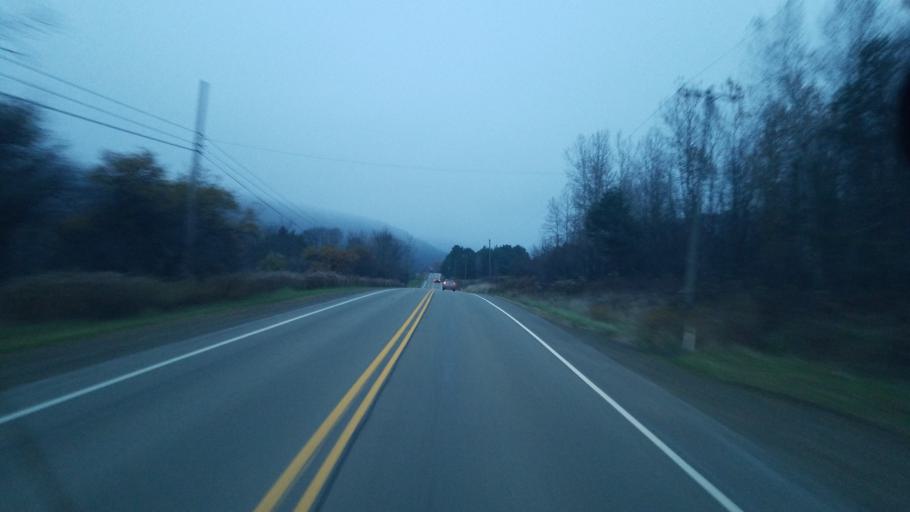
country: US
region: Pennsylvania
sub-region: McKean County
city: Smethport
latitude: 41.7556
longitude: -78.5237
